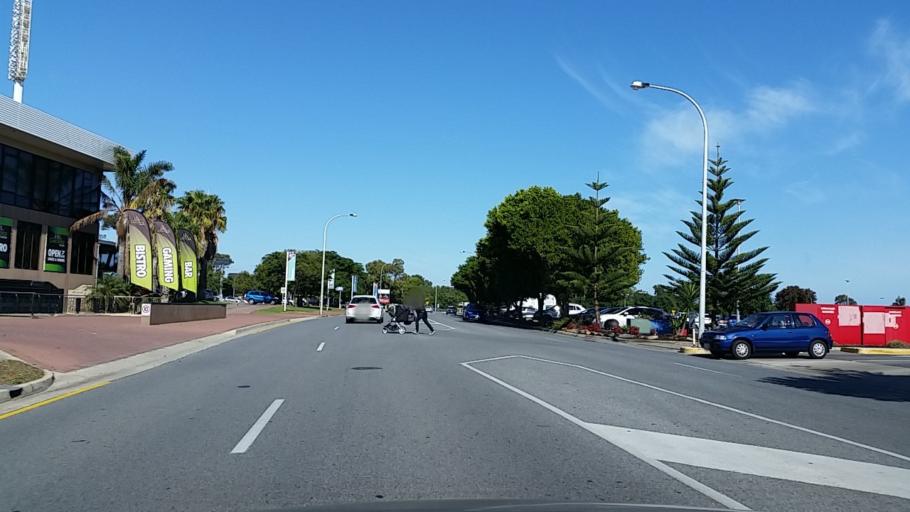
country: AU
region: South Australia
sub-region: Charles Sturt
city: Royal Park
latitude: -34.8795
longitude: 138.4935
